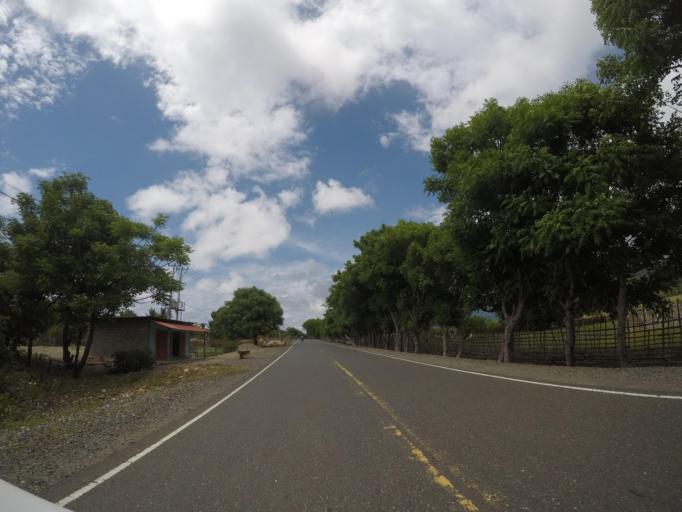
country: TL
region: Liquica
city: Maubara
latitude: -8.7732
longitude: 125.1007
